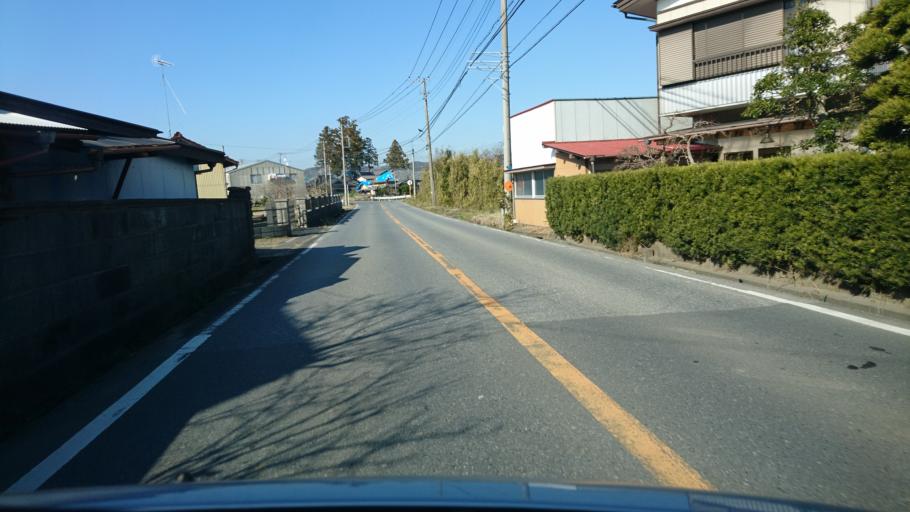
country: JP
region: Chiba
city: Kimitsu
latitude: 35.3009
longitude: 139.9747
